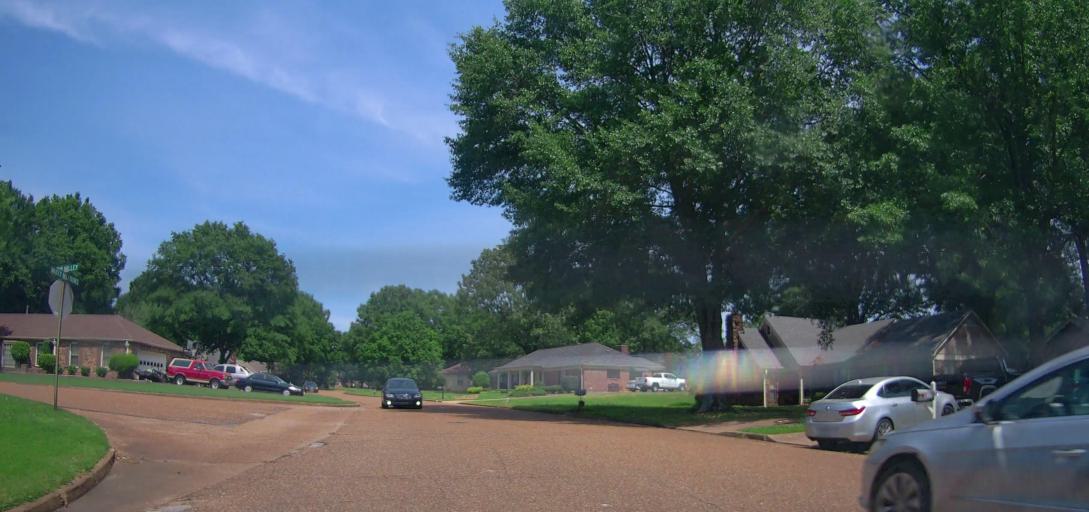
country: US
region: Tennessee
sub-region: Shelby County
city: Germantown
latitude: 35.0441
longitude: -89.7914
